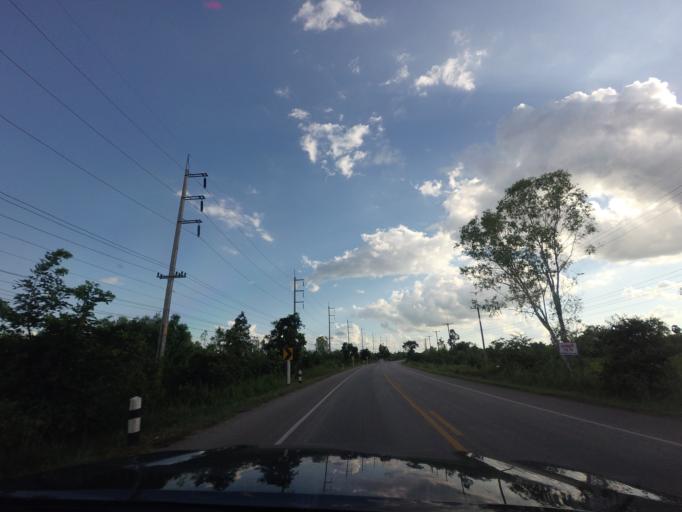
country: TH
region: Changwat Udon Thani
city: Thung Fon
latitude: 17.4694
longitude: 103.1931
